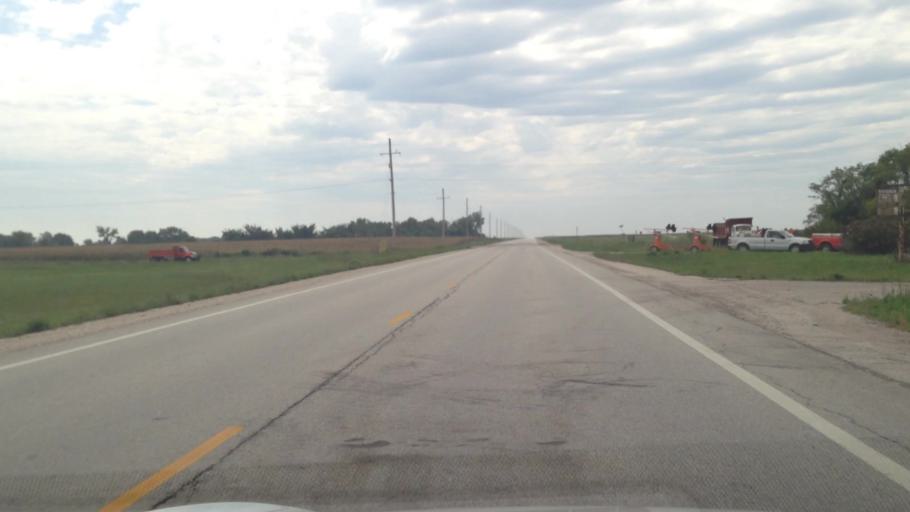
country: US
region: Kansas
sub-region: Anderson County
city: Garnett
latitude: 38.0682
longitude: -95.1694
